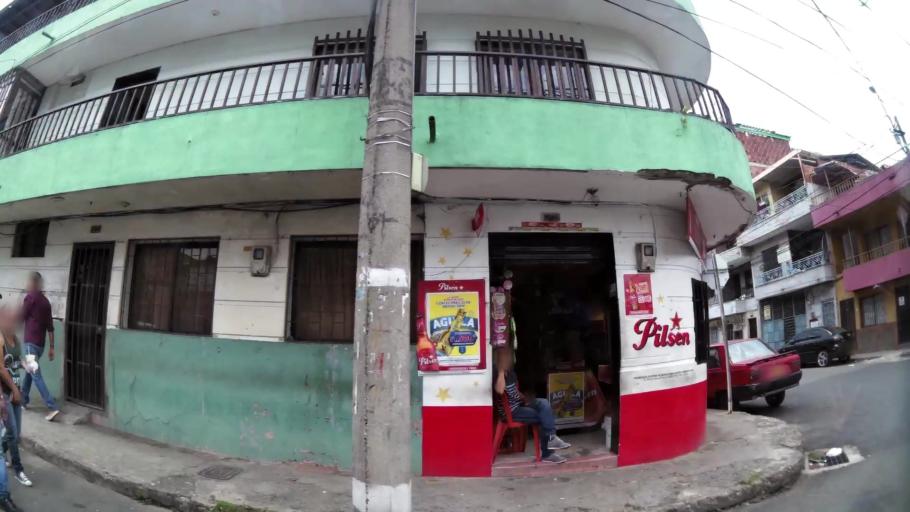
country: CO
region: Antioquia
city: Envigado
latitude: 6.1706
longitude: -75.6063
